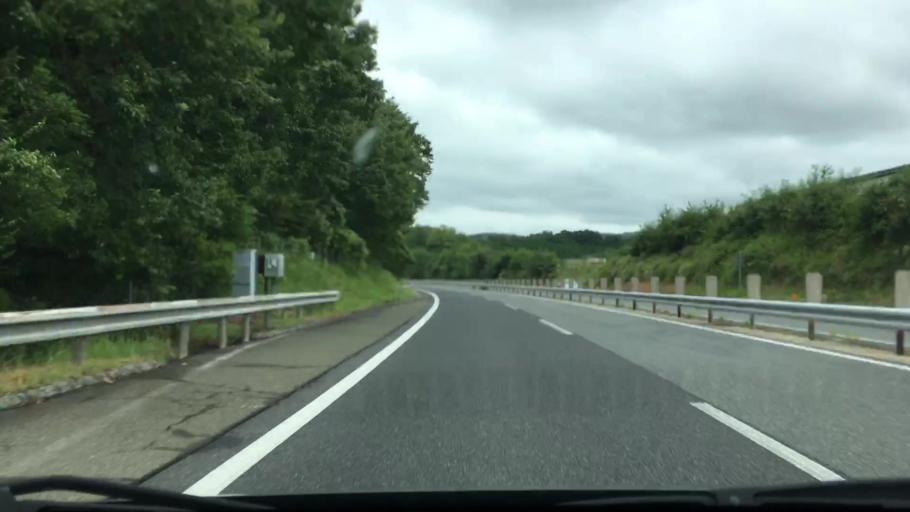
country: JP
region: Hiroshima
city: Shobara
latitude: 34.8375
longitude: 133.0446
